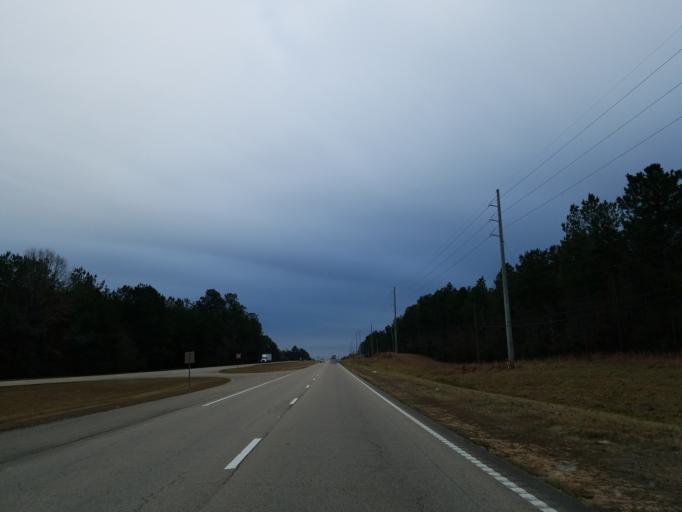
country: US
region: Mississippi
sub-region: Forrest County
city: Hattiesburg
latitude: 31.2597
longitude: -89.2822
